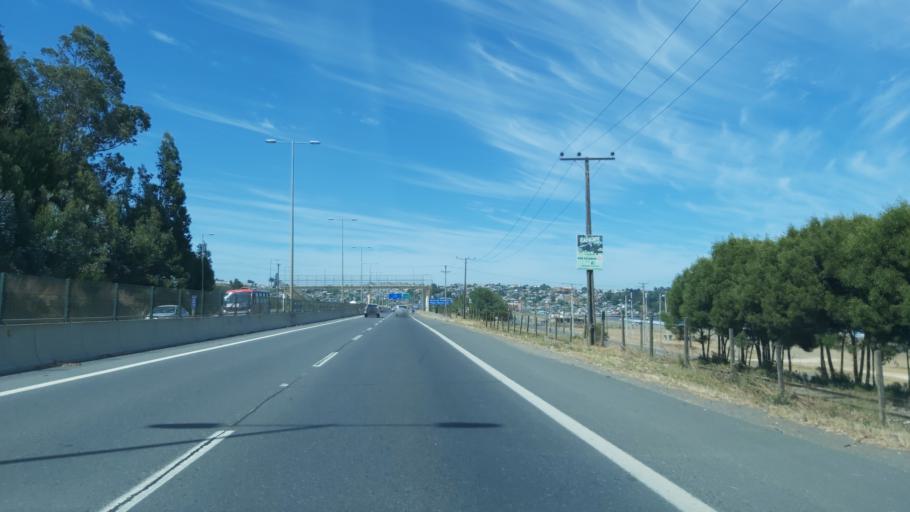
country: CL
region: Biobio
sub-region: Provincia de Concepcion
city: Lota
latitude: -37.0653
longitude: -73.1428
